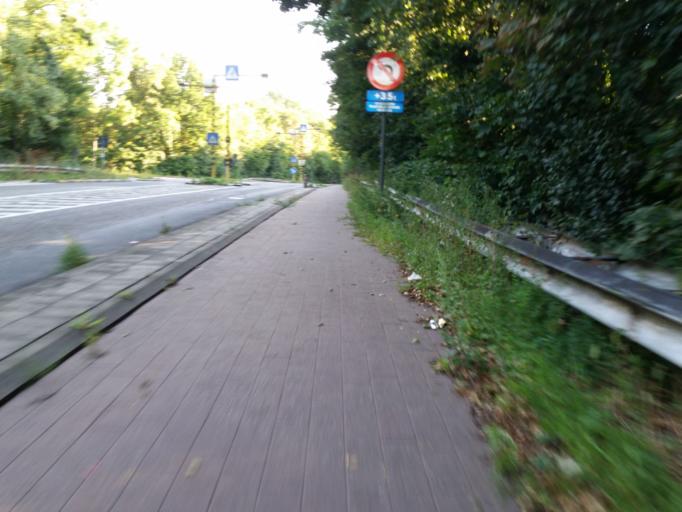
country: BE
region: Flanders
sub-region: Provincie Vlaams-Brabant
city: Machelen
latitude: 50.9254
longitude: 4.4642
